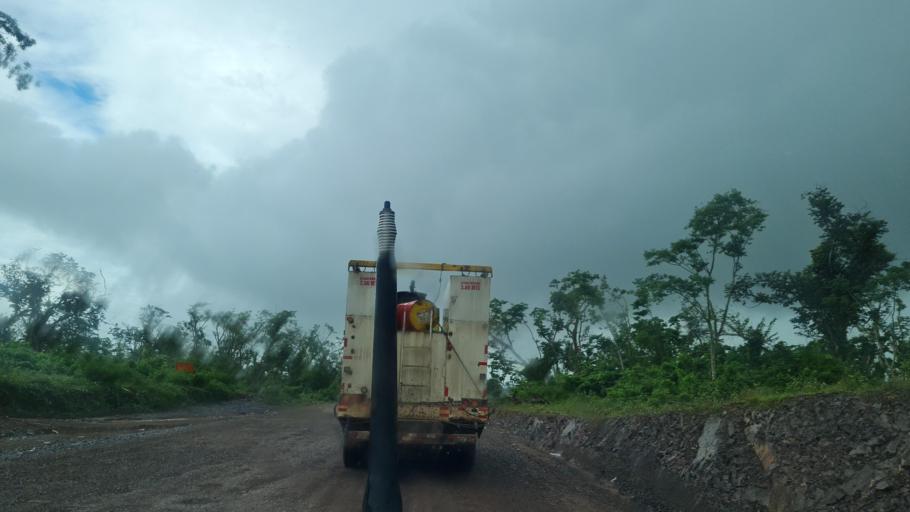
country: NI
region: Atlantico Norte (RAAN)
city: Siuna
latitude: 13.7014
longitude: -84.4445
